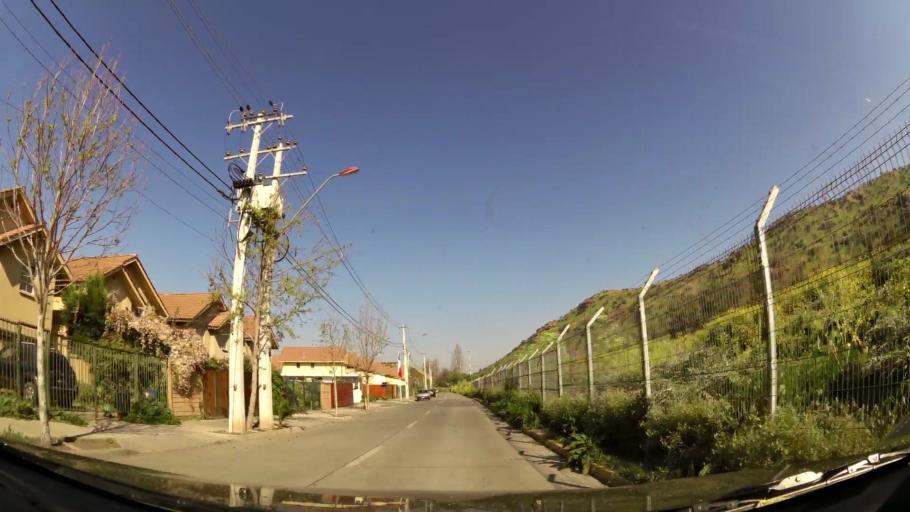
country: CL
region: Santiago Metropolitan
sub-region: Provincia de Chacabuco
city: Chicureo Abajo
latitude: -33.3520
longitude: -70.6851
